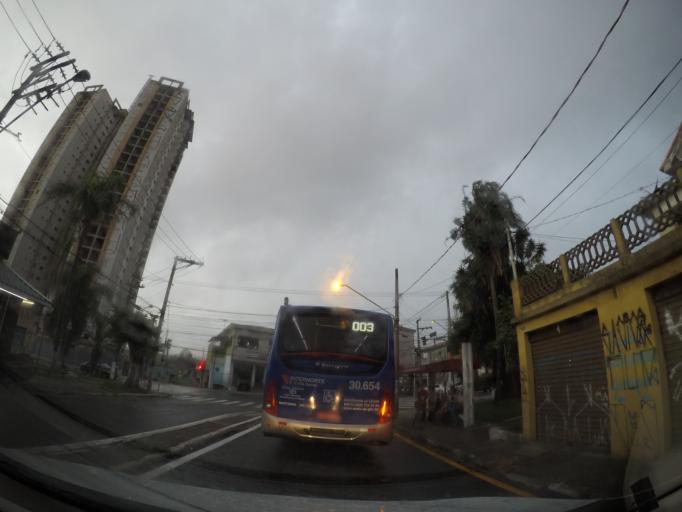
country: BR
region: Sao Paulo
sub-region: Guarulhos
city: Guarulhos
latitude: -23.4630
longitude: -46.5552
